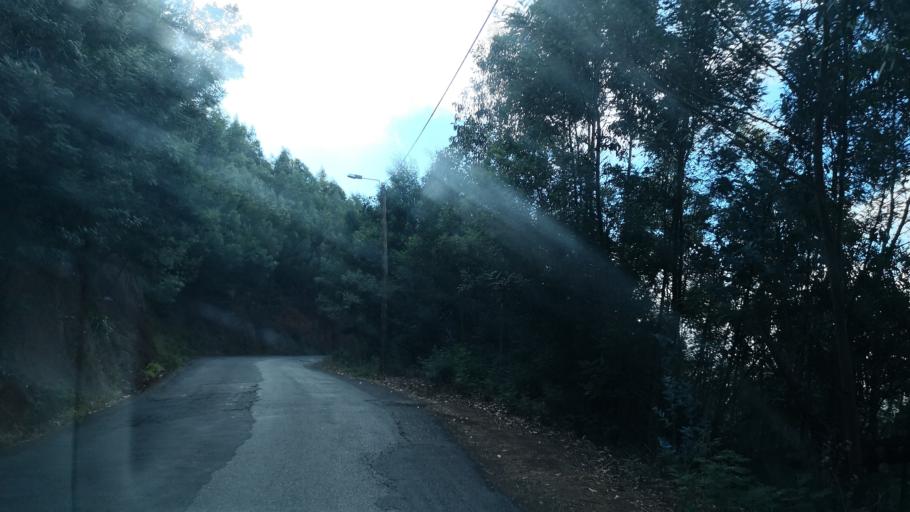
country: PT
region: Madeira
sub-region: Santa Cruz
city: Camacha
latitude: 32.6683
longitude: -16.8372
